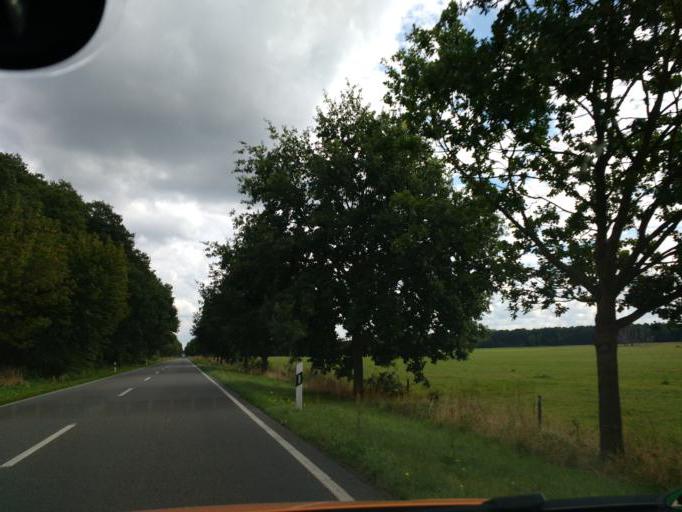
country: DE
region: Brandenburg
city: Marienwerder
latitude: 52.8549
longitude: 13.5612
